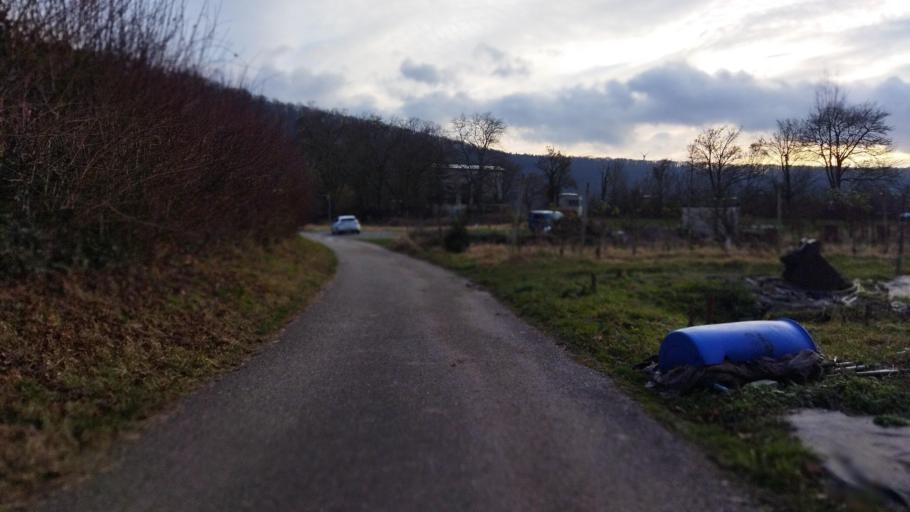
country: DE
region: Baden-Wuerttemberg
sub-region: Regierungsbezirk Stuttgart
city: Hessigheim
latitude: 48.9948
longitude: 9.1943
